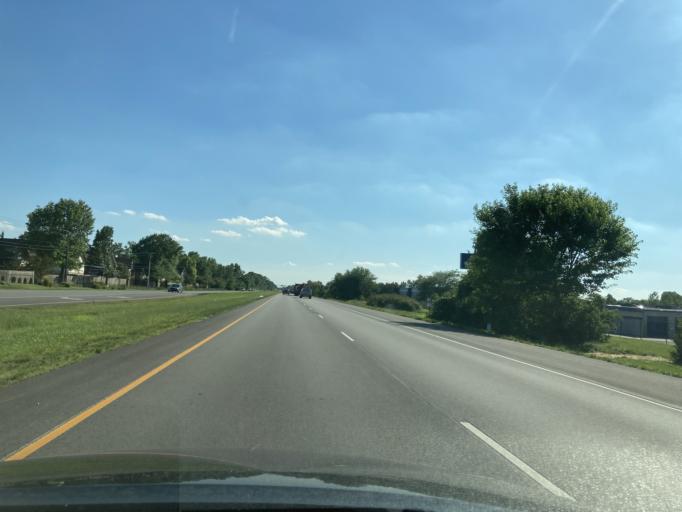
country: US
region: Indiana
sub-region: Marion County
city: Lawrence
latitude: 39.8802
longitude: -86.0710
